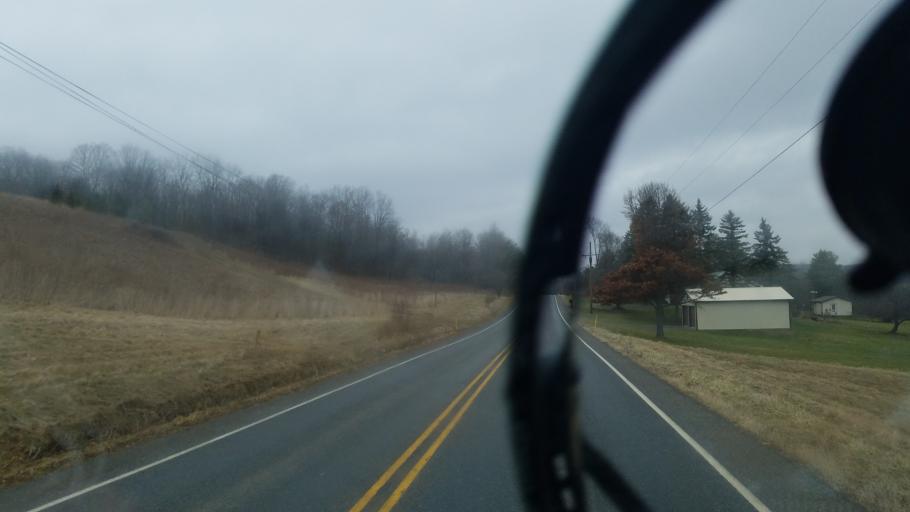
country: US
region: New York
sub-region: Allegany County
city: Wellsville
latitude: 41.9758
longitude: -77.8618
